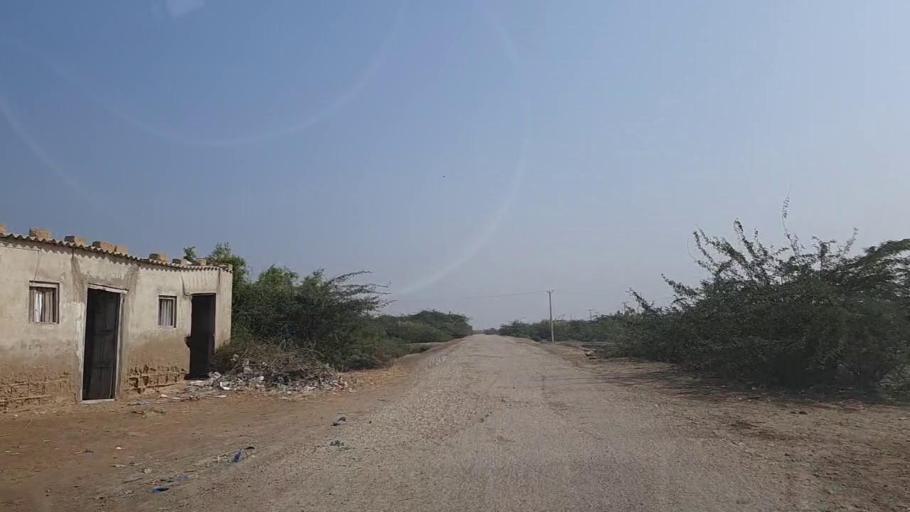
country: PK
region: Sindh
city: Keti Bandar
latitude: 24.2548
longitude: 67.6219
